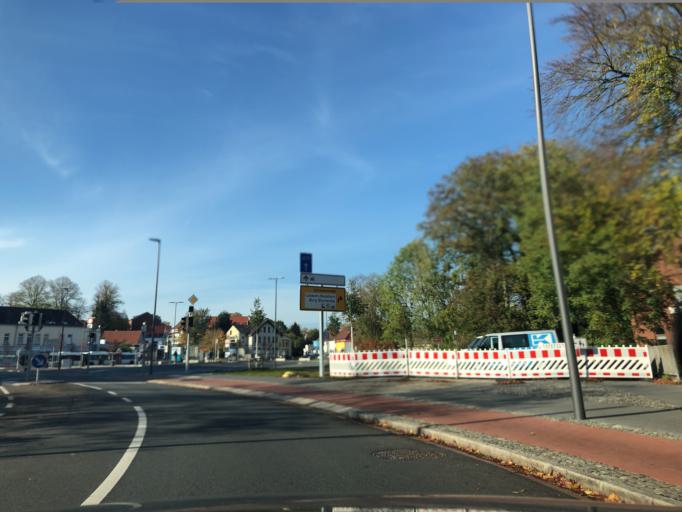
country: DE
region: Lower Saxony
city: Lemwerder
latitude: 53.1831
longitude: 8.5816
